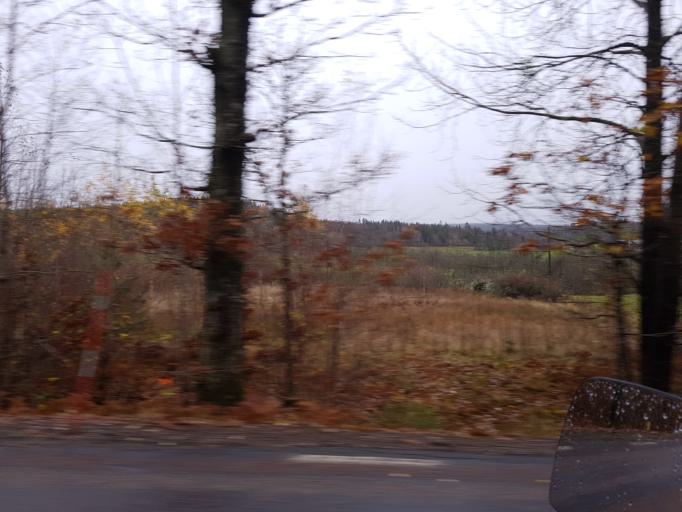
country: SE
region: Vaestra Goetaland
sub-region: Orust
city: Henan
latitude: 58.2630
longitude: 11.7391
